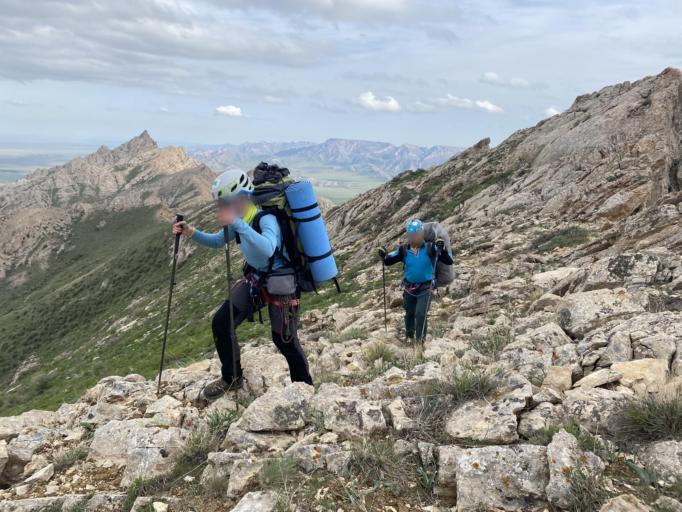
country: KZ
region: Ongtustik Qazaqstan
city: Ashchysay
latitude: 43.7559
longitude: 68.8160
